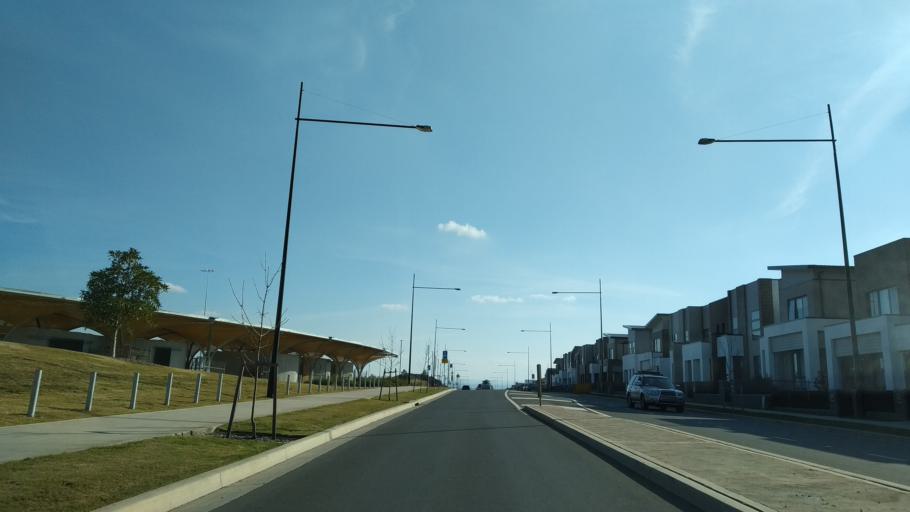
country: AU
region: New South Wales
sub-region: Blacktown
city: Hassall Grove
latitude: -33.6952
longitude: 150.8185
